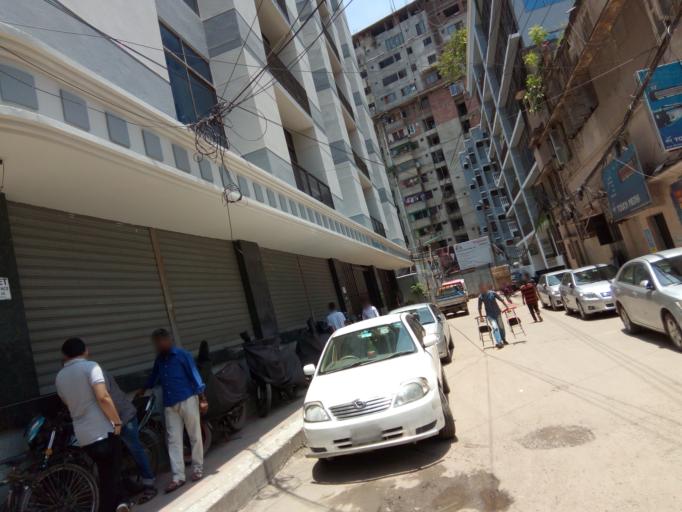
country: BD
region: Dhaka
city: Paltan
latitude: 23.7315
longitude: 90.4123
